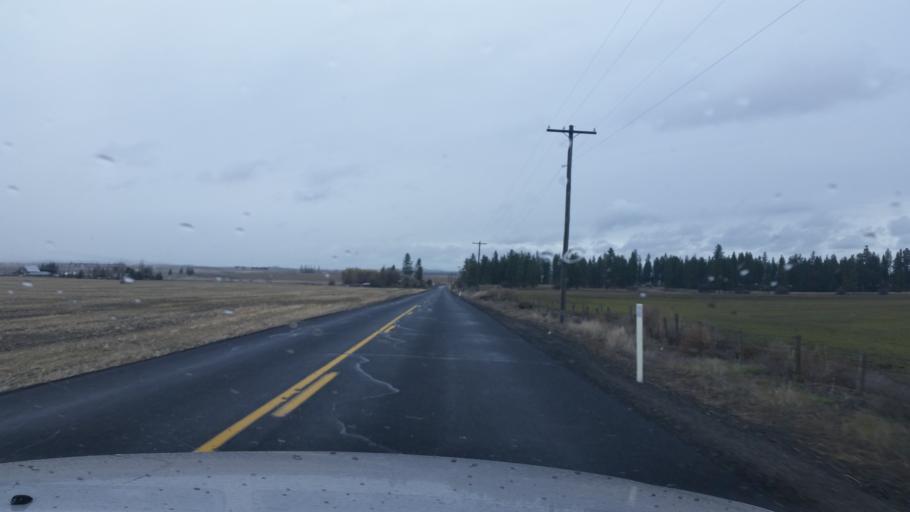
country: US
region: Washington
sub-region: Spokane County
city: Medical Lake
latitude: 47.6073
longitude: -117.7368
